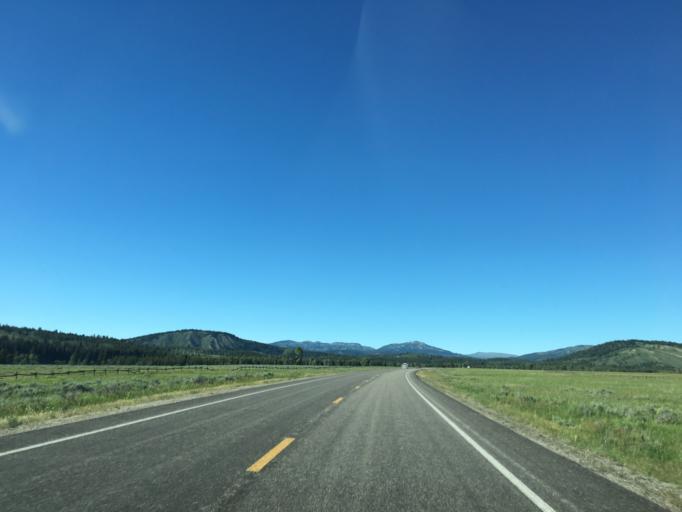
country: US
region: Wyoming
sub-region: Teton County
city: Jackson
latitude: 43.8166
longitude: -110.5254
